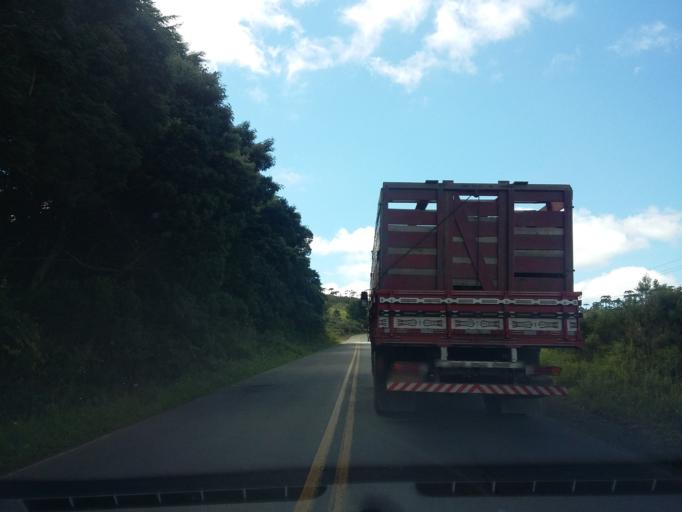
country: BR
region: Santa Catarina
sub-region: Sao Joaquim
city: Sao Joaquim
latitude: -28.2376
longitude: -49.8194
